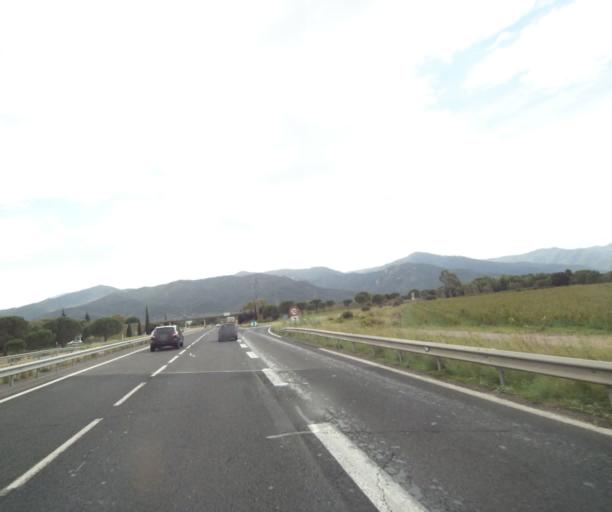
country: FR
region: Languedoc-Roussillon
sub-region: Departement des Pyrenees-Orientales
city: Argelers
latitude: 42.5528
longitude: 3.0060
